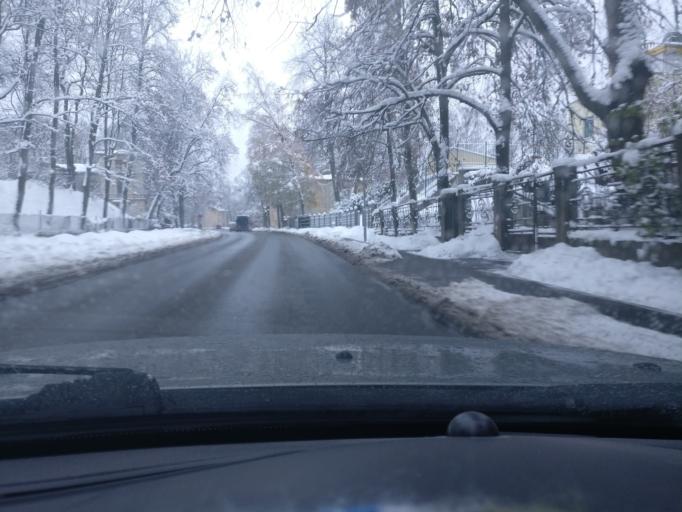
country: LV
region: Riga
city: Riga
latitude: 56.9297
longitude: 24.0811
